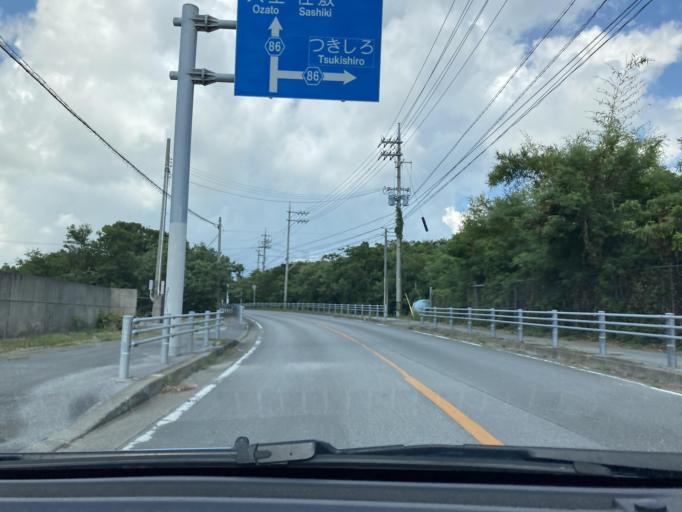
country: JP
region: Okinawa
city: Tomigusuku
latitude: 26.1521
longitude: 127.7908
